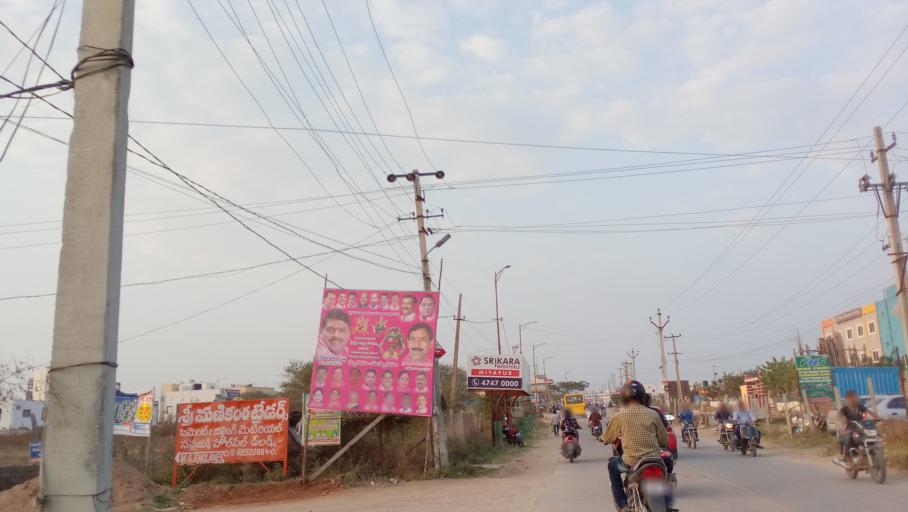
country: IN
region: Telangana
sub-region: Medak
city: Serilingampalle
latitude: 17.5150
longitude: 78.3190
